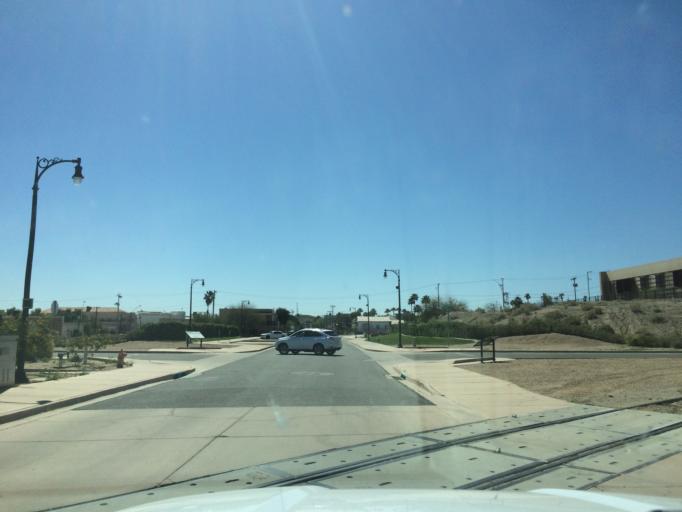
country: US
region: Arizona
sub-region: Yuma County
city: Yuma
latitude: 32.7268
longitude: -114.6197
